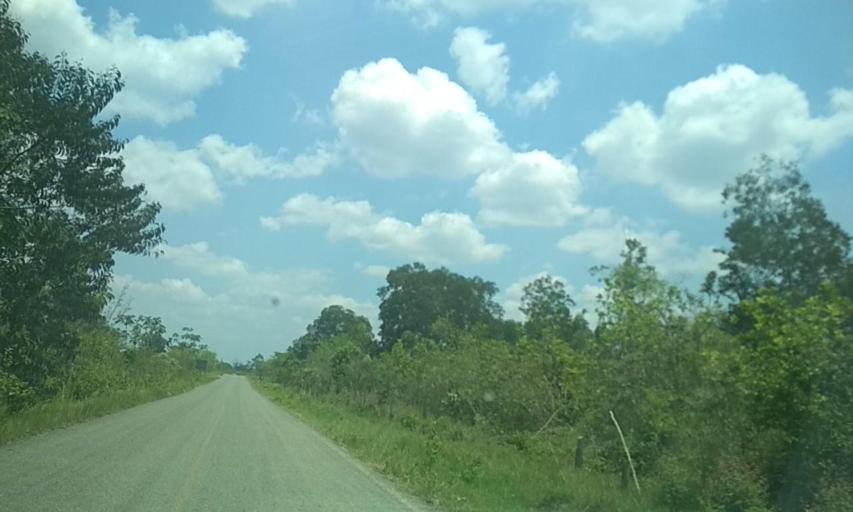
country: MX
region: Tabasco
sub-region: Huimanguillo
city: Francisco Rueda
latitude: 17.7879
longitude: -93.8328
